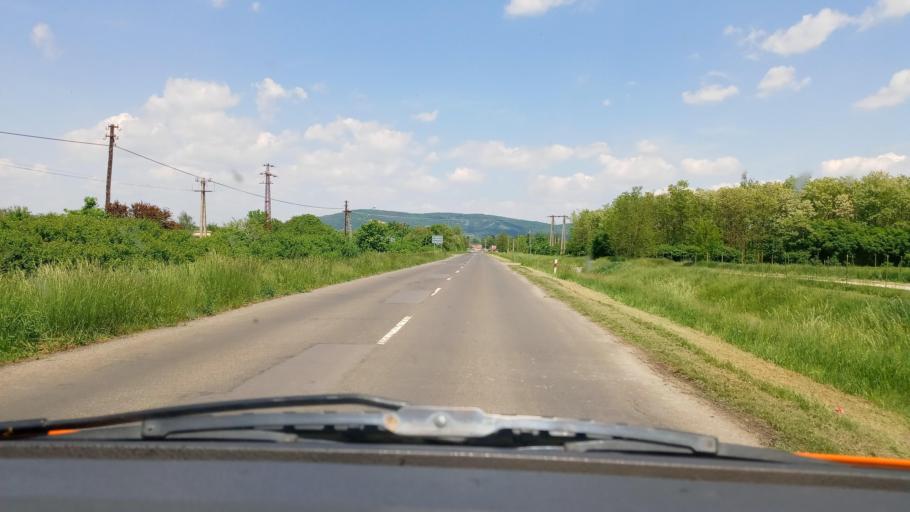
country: HU
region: Baranya
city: Harkany
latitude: 45.8384
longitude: 18.2292
